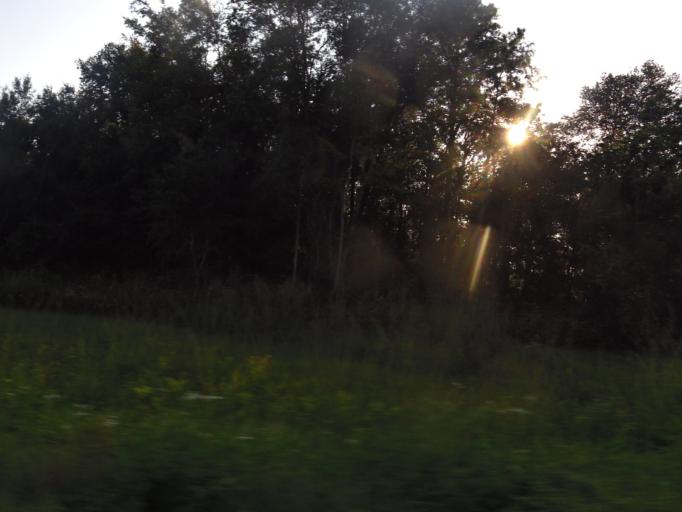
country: US
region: Florida
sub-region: Nassau County
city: Hilliard
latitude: 30.5523
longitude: -81.9909
